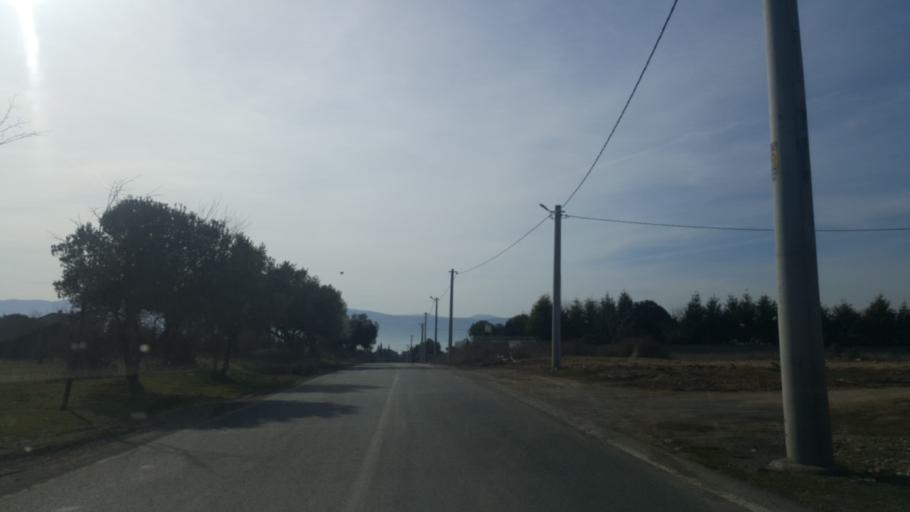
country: TR
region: Kocaeli
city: Tavsancil
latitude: 40.7832
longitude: 29.5739
